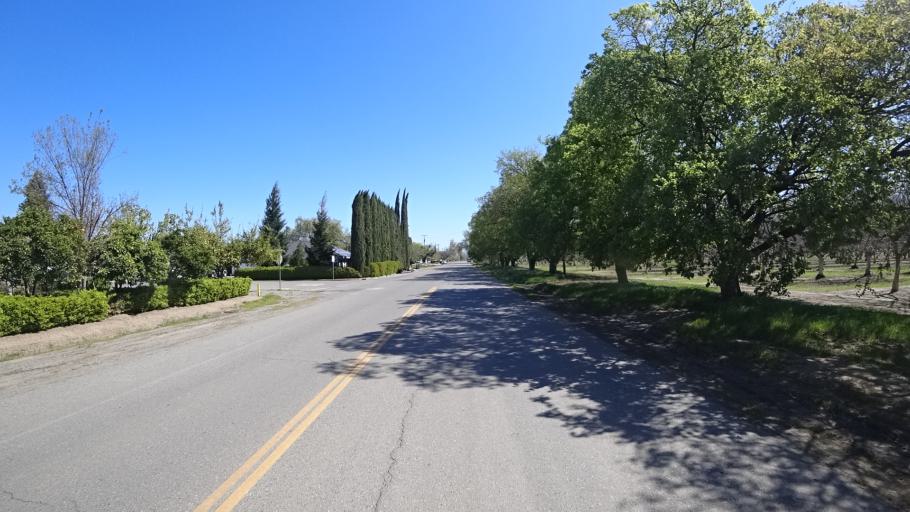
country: US
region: California
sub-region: Glenn County
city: Hamilton City
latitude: 39.7377
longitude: -122.0135
